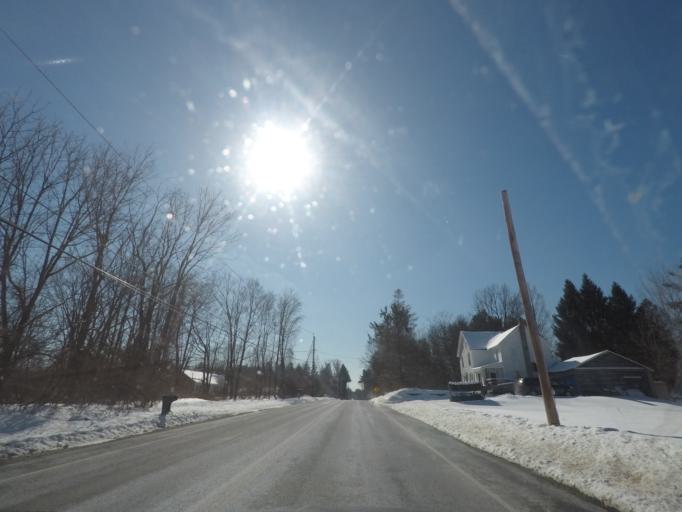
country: US
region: New York
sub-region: Saratoga County
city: Country Knolls
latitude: 42.9375
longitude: -73.8256
